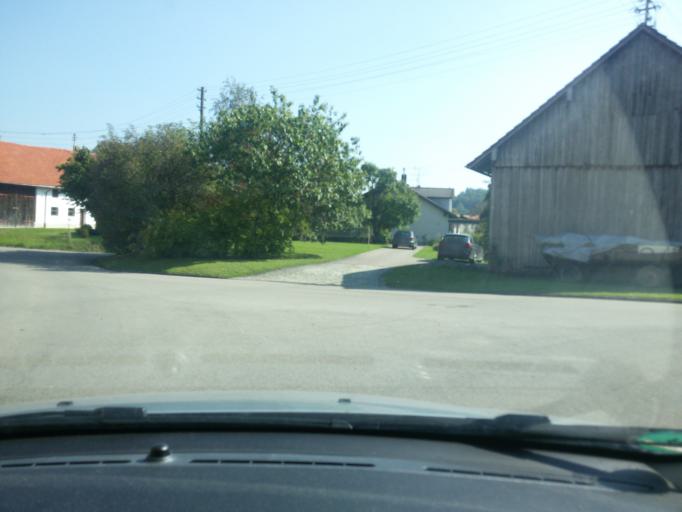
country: DE
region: Bavaria
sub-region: Swabia
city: Scherstetten
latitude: 48.1806
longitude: 10.6383
